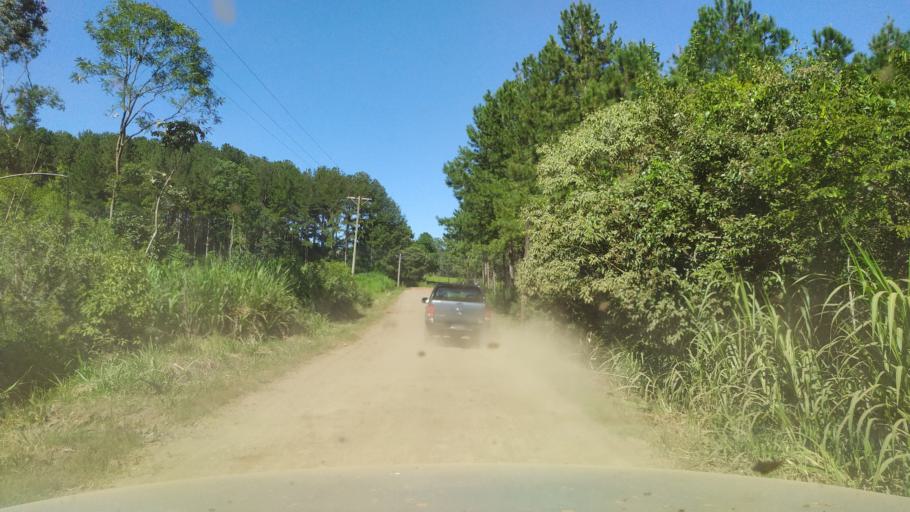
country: AR
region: Misiones
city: Caraguatay
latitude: -26.6839
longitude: -54.7114
